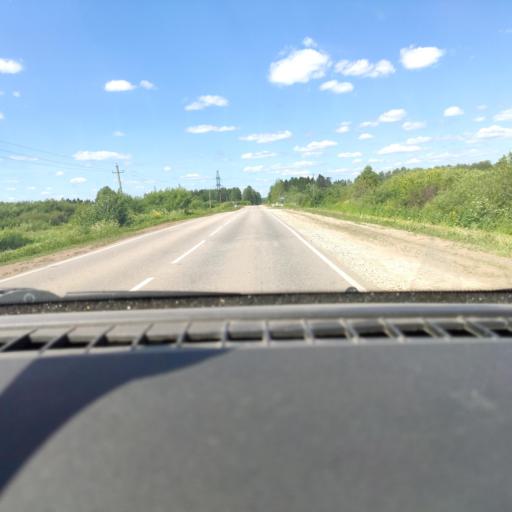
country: RU
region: Perm
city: Chaykovskaya
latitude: 58.0809
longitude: 55.6165
